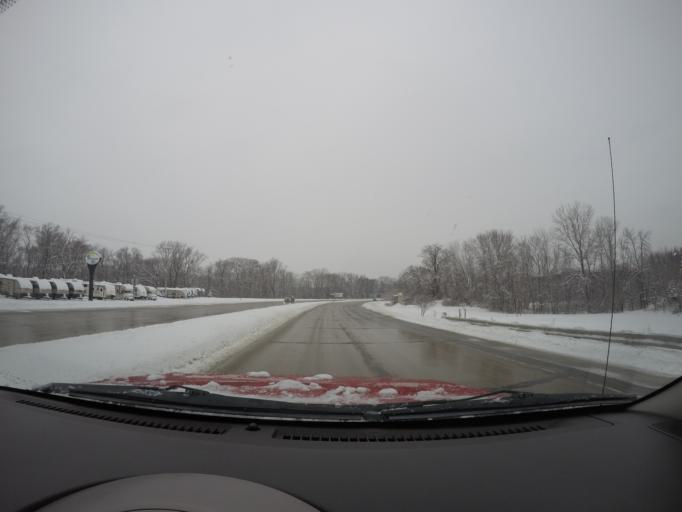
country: US
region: Minnesota
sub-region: Houston County
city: La Crescent
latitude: 43.8191
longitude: -91.2749
